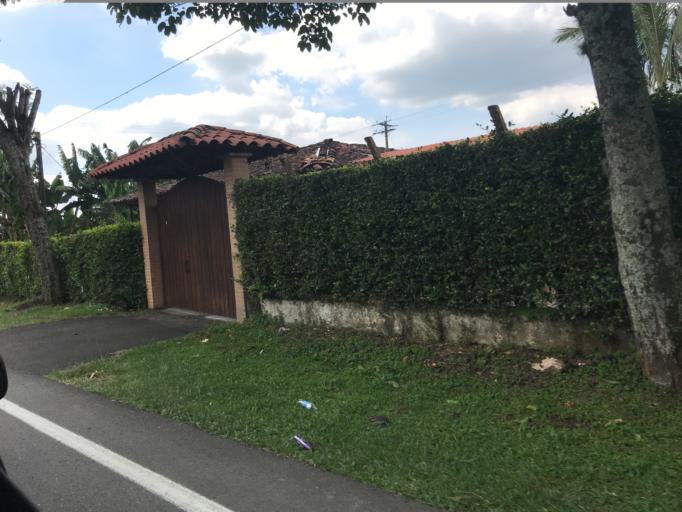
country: CO
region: Quindio
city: Armenia
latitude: 4.4896
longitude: -75.6940
